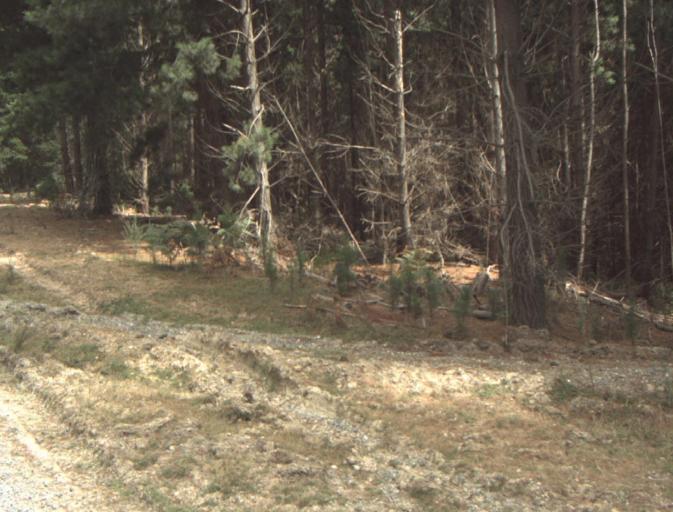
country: AU
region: Tasmania
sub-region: Launceston
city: Mayfield
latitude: -41.1721
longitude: 147.1996
